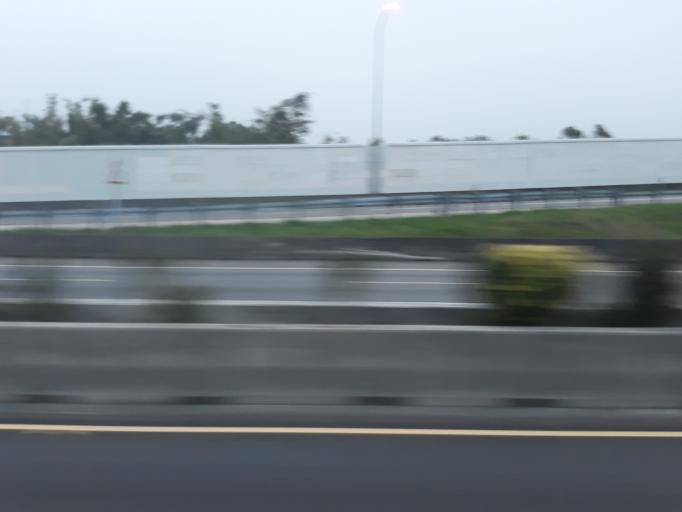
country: TW
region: Taiwan
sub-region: Hsinchu
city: Hsinchu
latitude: 24.6941
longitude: 120.9198
